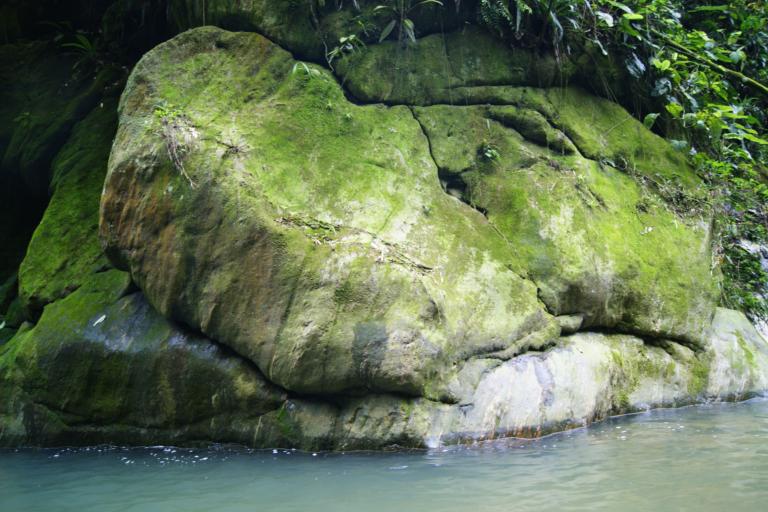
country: BR
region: Sao Paulo
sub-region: Rio Grande Da Serra
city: Rio Grande da Serra
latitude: -23.8115
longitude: -46.3565
